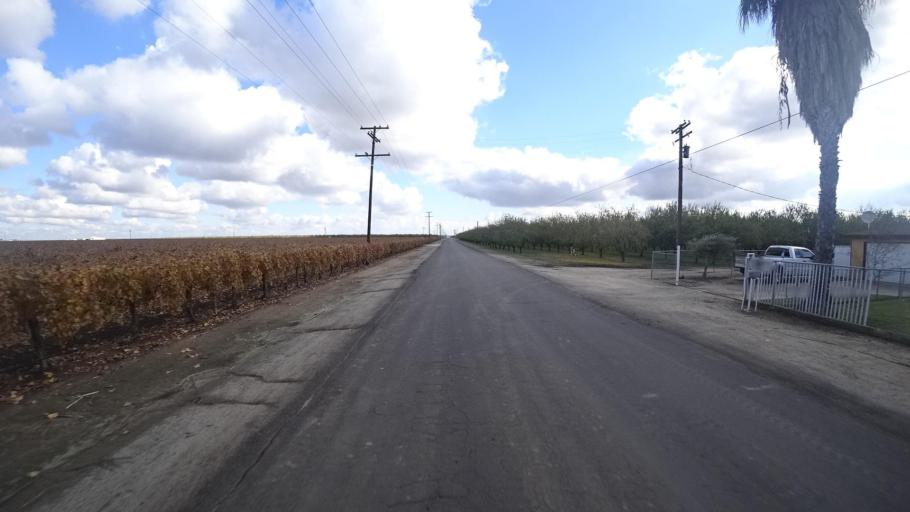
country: US
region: California
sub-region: Kern County
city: McFarland
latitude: 35.6601
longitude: -119.1990
